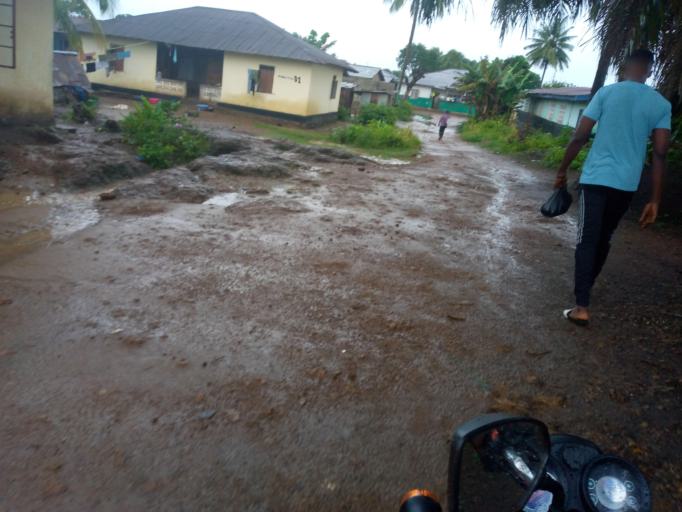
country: SL
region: Eastern Province
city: Kenema
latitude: 7.8839
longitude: -11.1800
